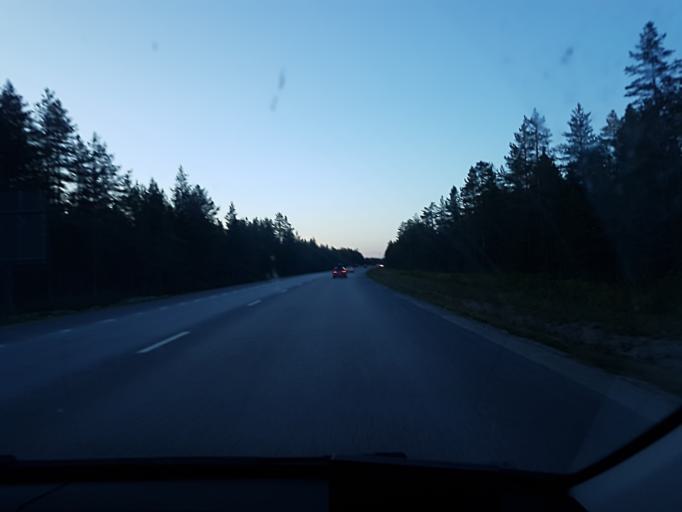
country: SE
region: Norrbotten
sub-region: Lulea Kommun
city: Bergnaset
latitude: 65.5698
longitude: 22.0740
